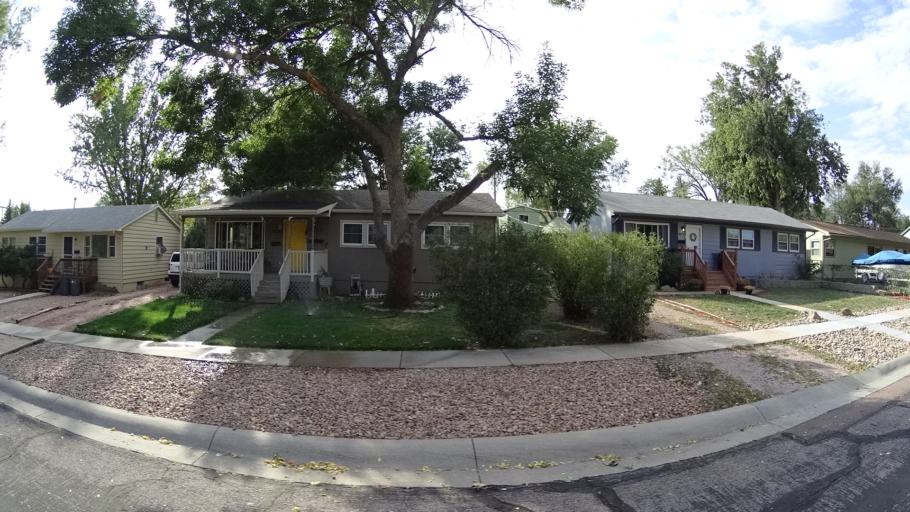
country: US
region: Colorado
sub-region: El Paso County
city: Colorado Springs
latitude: 38.8570
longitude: -104.7714
